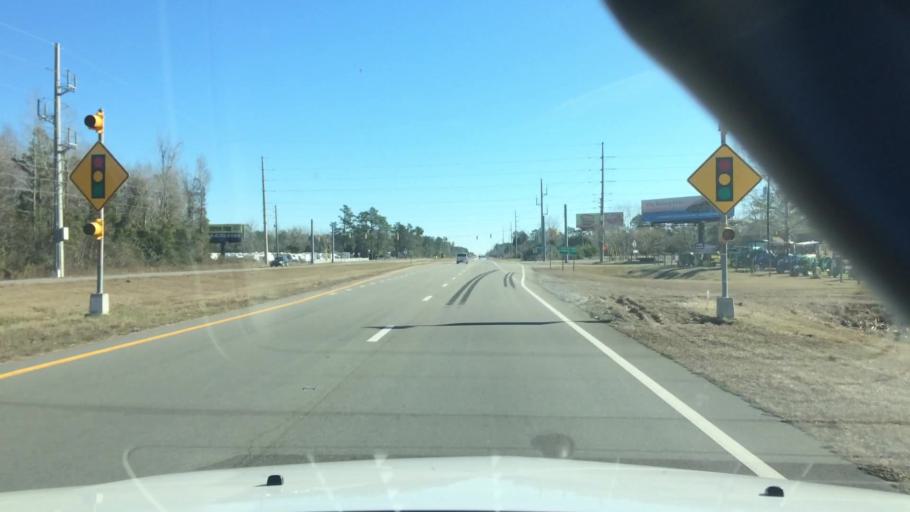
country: US
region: North Carolina
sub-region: Brunswick County
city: Carolina Shores
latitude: 33.9380
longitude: -78.5575
